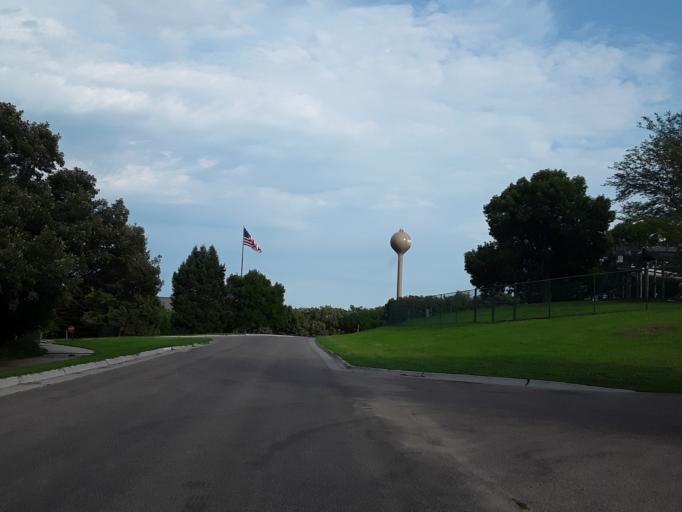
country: US
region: Nebraska
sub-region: Saunders County
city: Ashland
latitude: 41.0276
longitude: -96.3106
